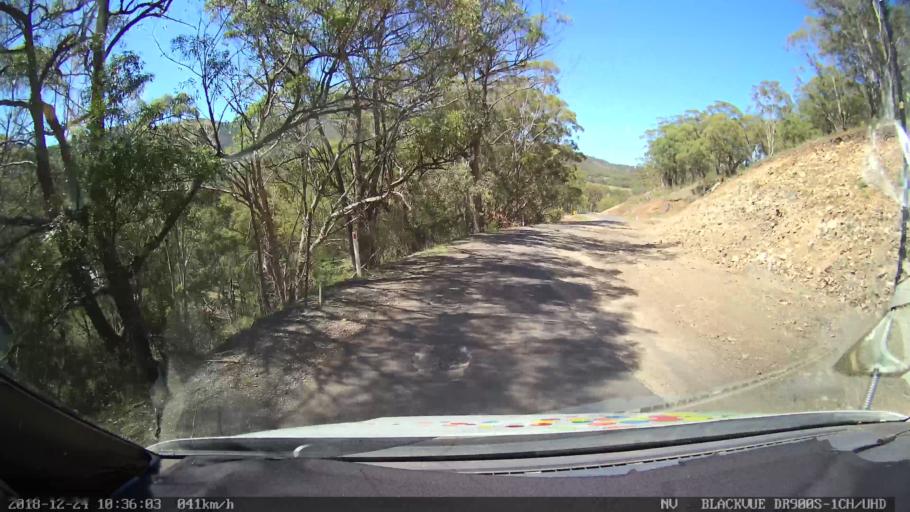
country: AU
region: New South Wales
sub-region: Upper Hunter Shire
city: Merriwa
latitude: -31.8422
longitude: 150.5010
